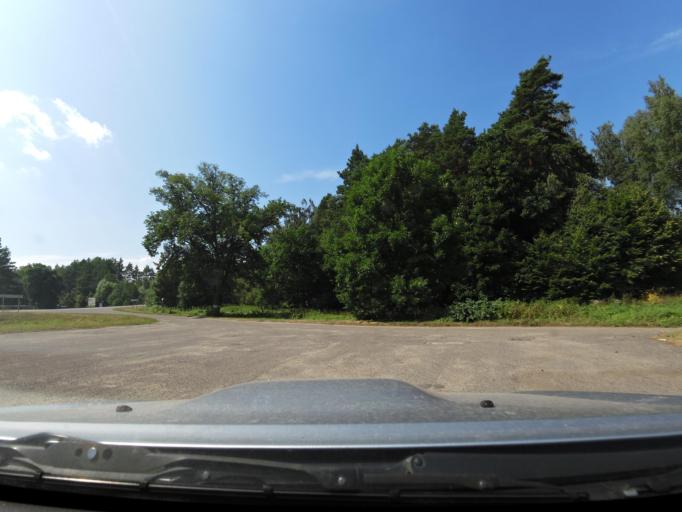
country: LT
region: Taurages apskritis
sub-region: Jurbarkas
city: Jurbarkas
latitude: 55.0828
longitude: 22.6011
